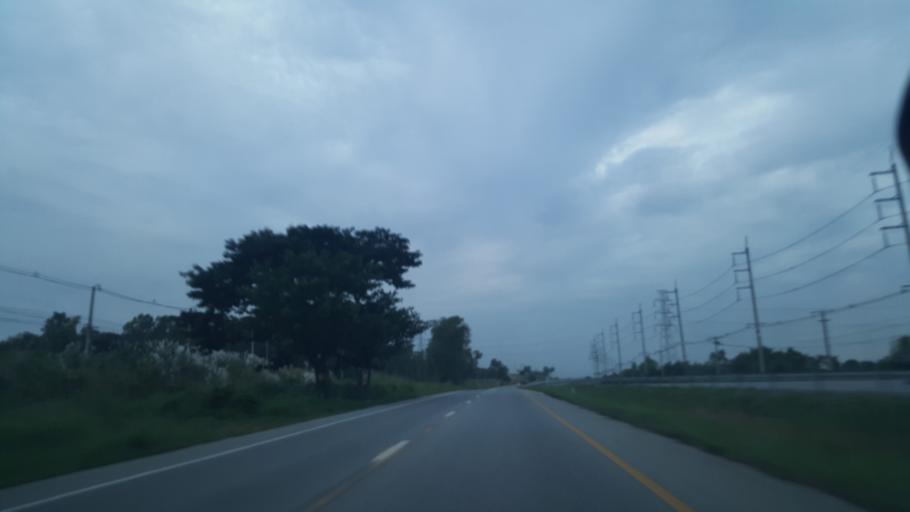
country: TH
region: Chon Buri
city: Ban Talat Bueng
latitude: 12.9324
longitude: 101.0368
